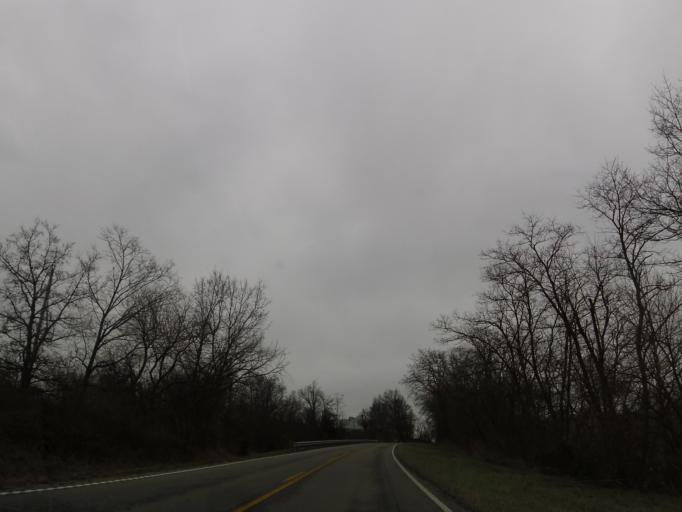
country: US
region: Kentucky
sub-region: Henry County
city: New Castle
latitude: 38.5069
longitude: -85.1827
